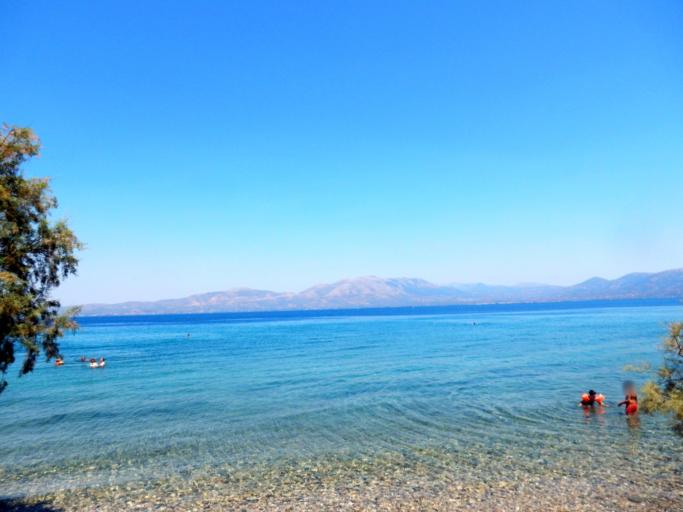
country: GR
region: Attica
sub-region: Nomarchia Anatolikis Attikis
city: Kalamos
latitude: 38.3075
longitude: 23.8593
